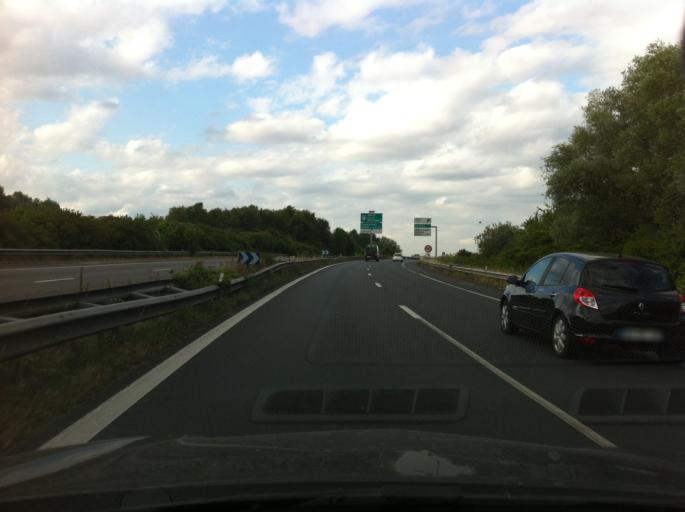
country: FR
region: Ile-de-France
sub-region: Departement de Seine-et-Marne
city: Servon
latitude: 48.7010
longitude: 2.5946
